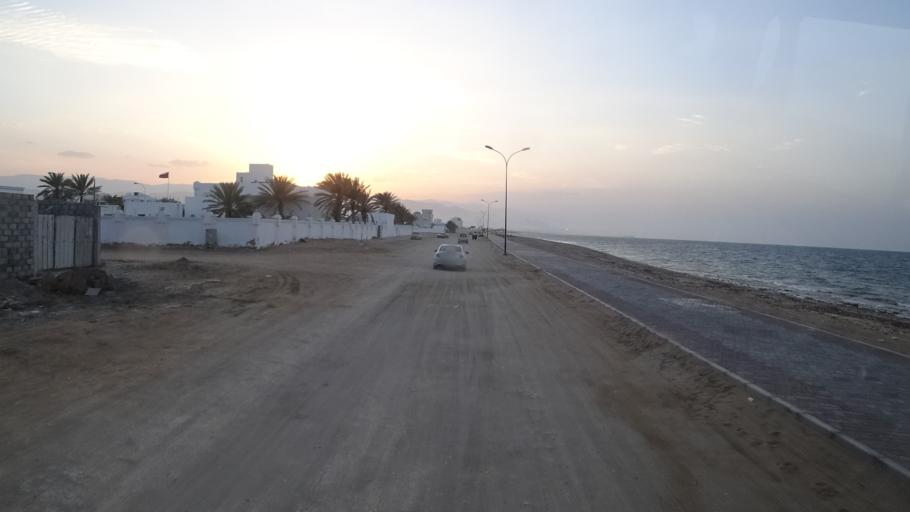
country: OM
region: Ash Sharqiyah
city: Sur
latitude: 22.5931
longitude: 59.4991
